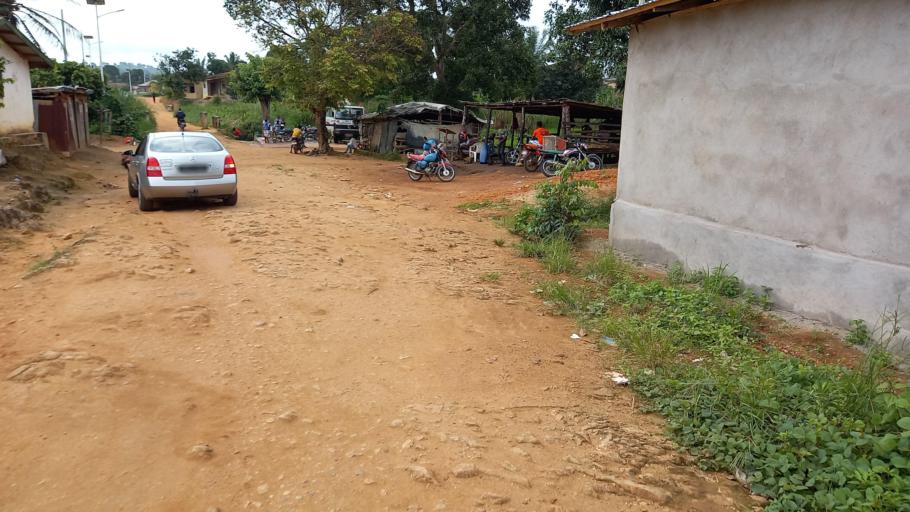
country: SL
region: Eastern Province
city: Kailahun
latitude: 8.2818
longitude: -10.5741
